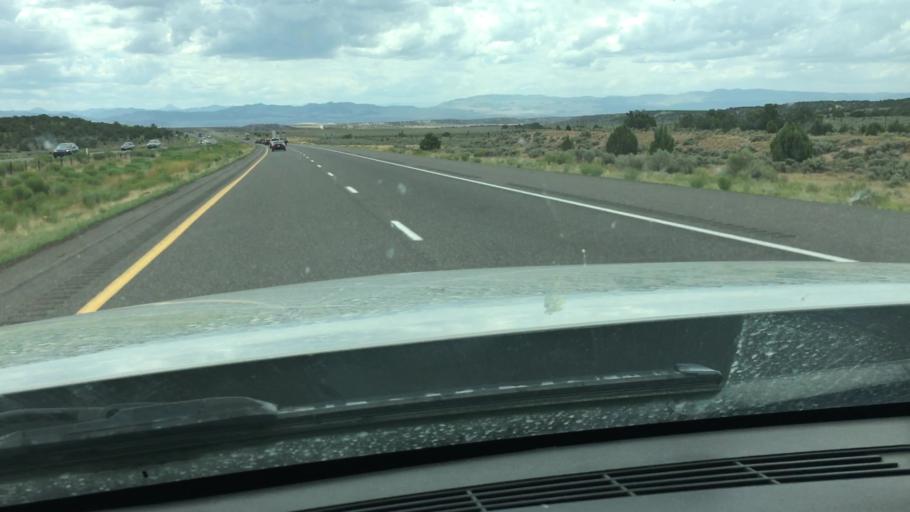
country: US
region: Utah
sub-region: Beaver County
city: Beaver
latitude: 38.3733
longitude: -112.6626
